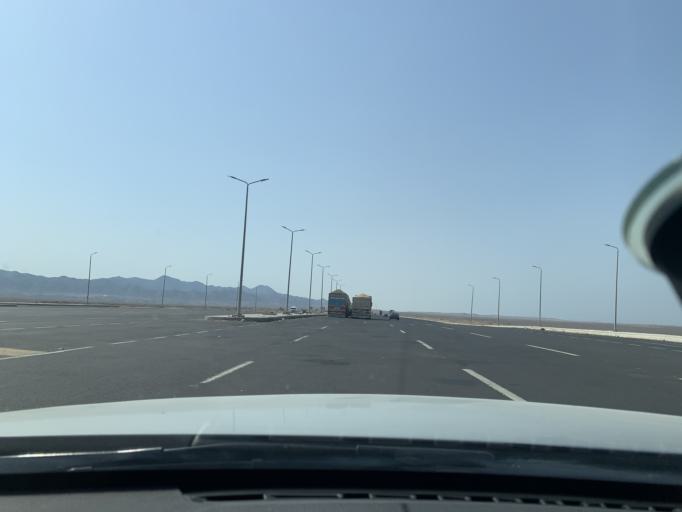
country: EG
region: Red Sea
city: El Gouna
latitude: 27.4312
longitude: 33.6091
